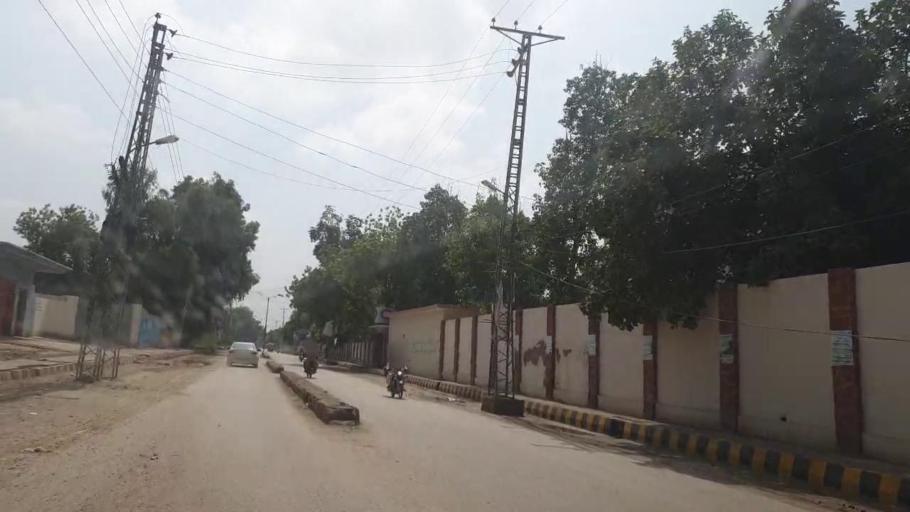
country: PK
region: Sindh
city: Khairpur
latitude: 27.5239
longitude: 68.7450
